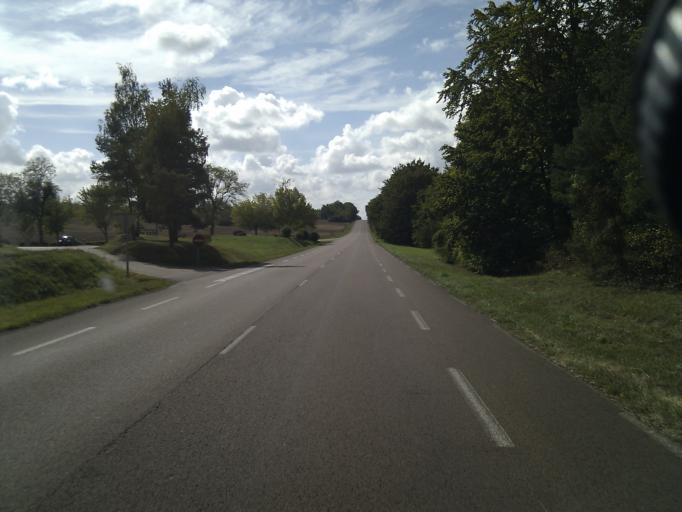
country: FR
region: Bourgogne
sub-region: Departement de la Cote-d'Or
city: Chatillon-sur-Seine
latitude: 47.8265
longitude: 4.5410
